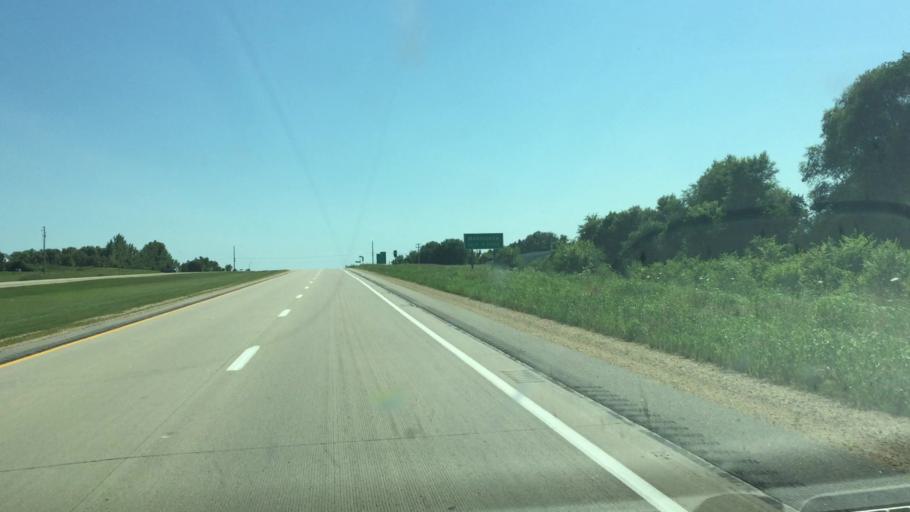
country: US
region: Iowa
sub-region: Jones County
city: Monticello
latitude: 42.2551
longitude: -91.1577
